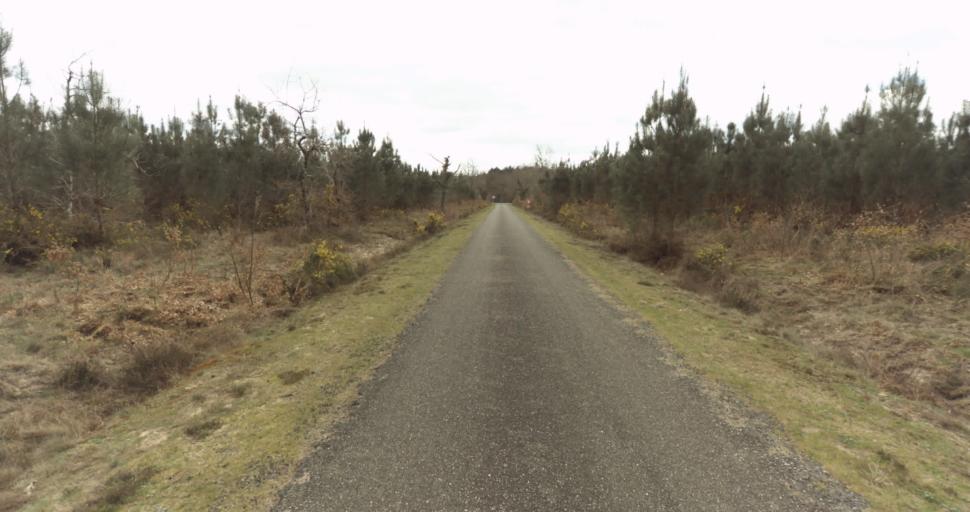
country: FR
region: Aquitaine
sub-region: Departement des Landes
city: Roquefort
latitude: 44.0785
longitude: -0.4403
